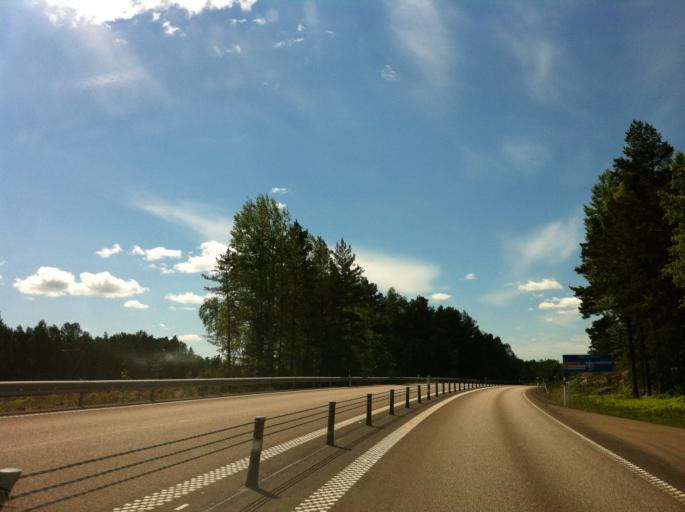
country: SE
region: Vaestra Goetaland
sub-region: Melleruds Kommun
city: Mellerud
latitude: 58.8613
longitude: 12.5593
